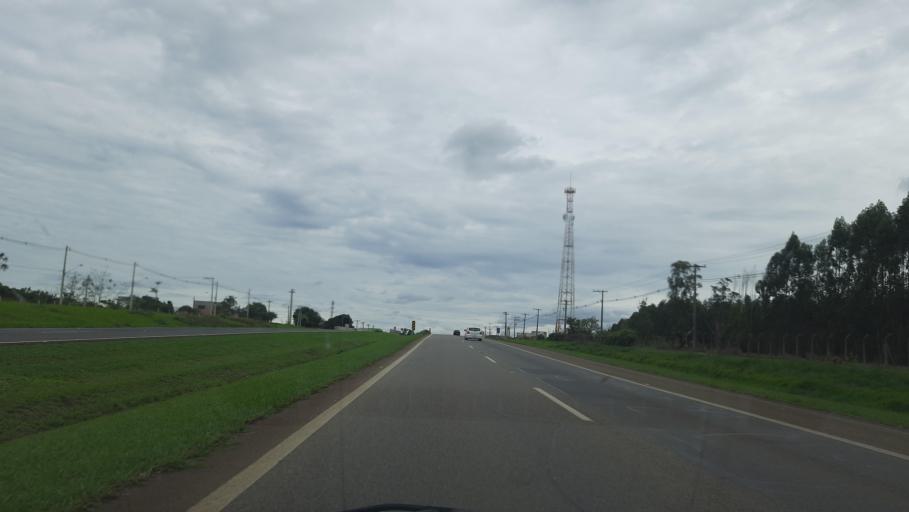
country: BR
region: Sao Paulo
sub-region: Moji-Guacu
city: Mogi-Gaucu
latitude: -22.3374
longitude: -46.9586
